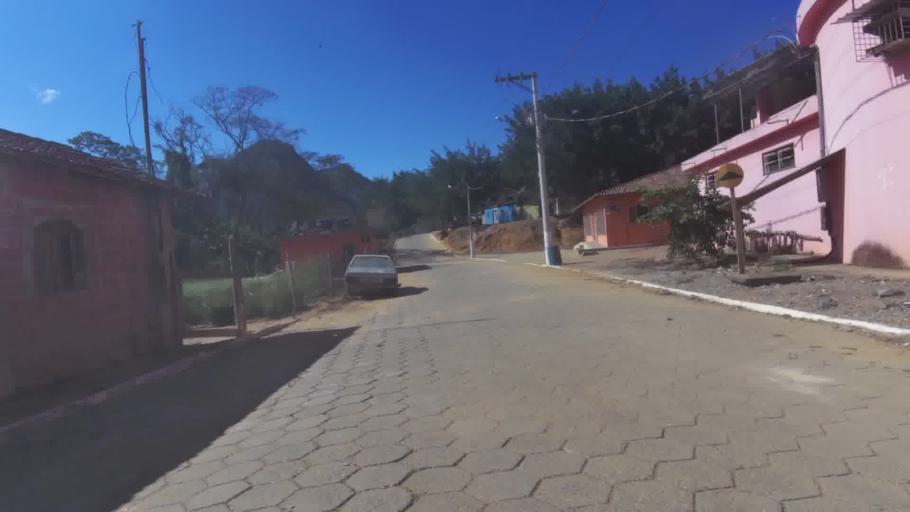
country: BR
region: Espirito Santo
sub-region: Cachoeiro De Itapemirim
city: Cachoeiro de Itapemirim
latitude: -20.9203
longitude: -41.1968
